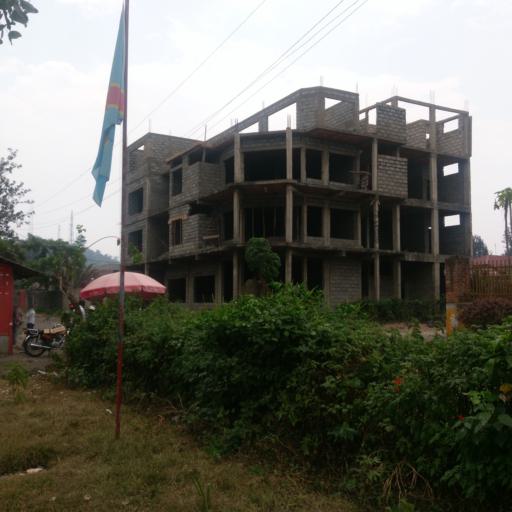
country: CD
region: Nord Kivu
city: Goma
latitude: -1.6847
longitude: 29.2326
